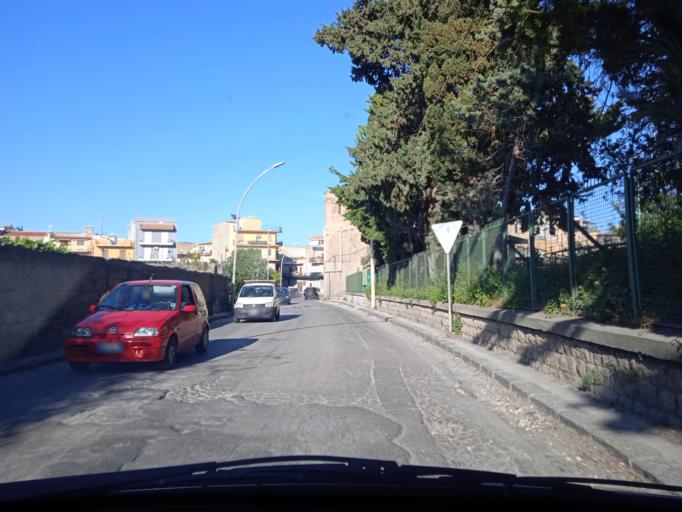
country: IT
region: Sicily
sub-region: Palermo
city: Villabate
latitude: 38.0878
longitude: 13.4511
